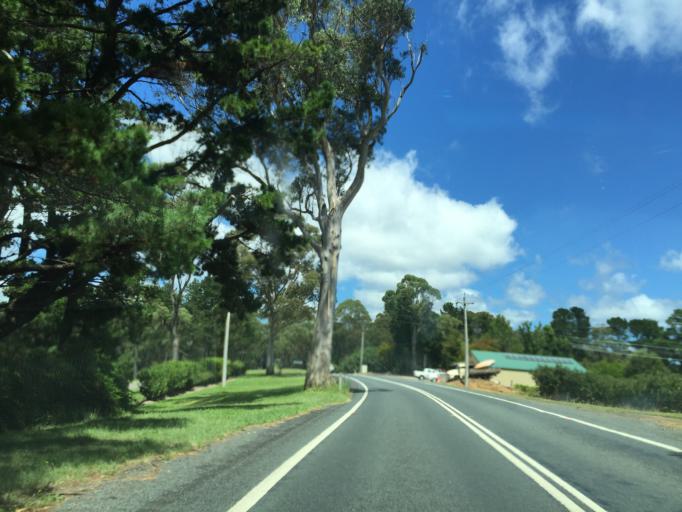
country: AU
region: New South Wales
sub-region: Blue Mountains Municipality
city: Lawson
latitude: -33.5210
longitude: 150.4623
